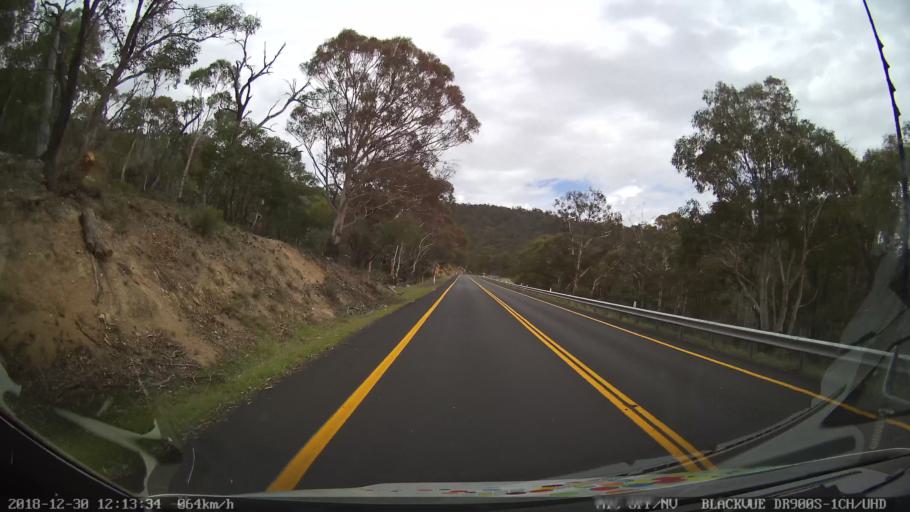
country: AU
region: New South Wales
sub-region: Snowy River
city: Jindabyne
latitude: -36.3480
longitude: 148.5838
